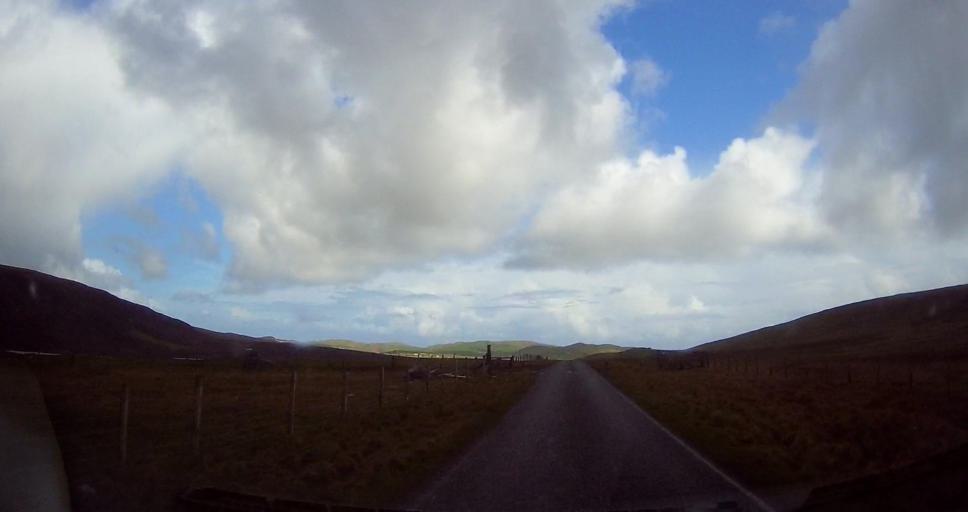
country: GB
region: Scotland
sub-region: Shetland Islands
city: Lerwick
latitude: 60.5609
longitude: -1.3358
